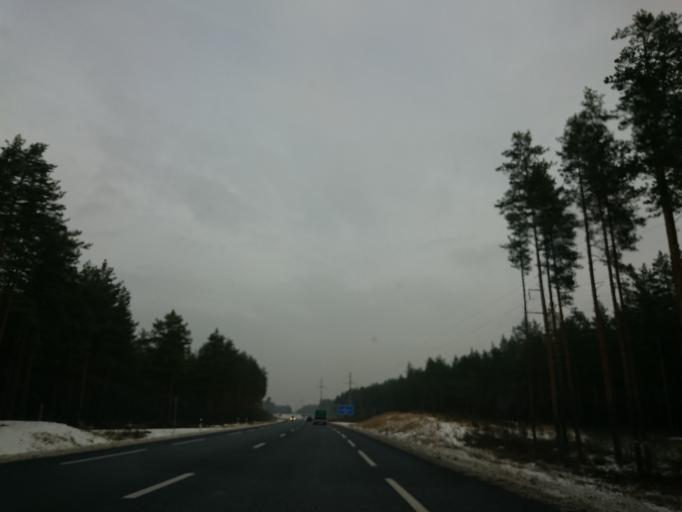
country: LV
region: Saulkrastu
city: Saulkrasti
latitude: 57.2372
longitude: 24.4272
